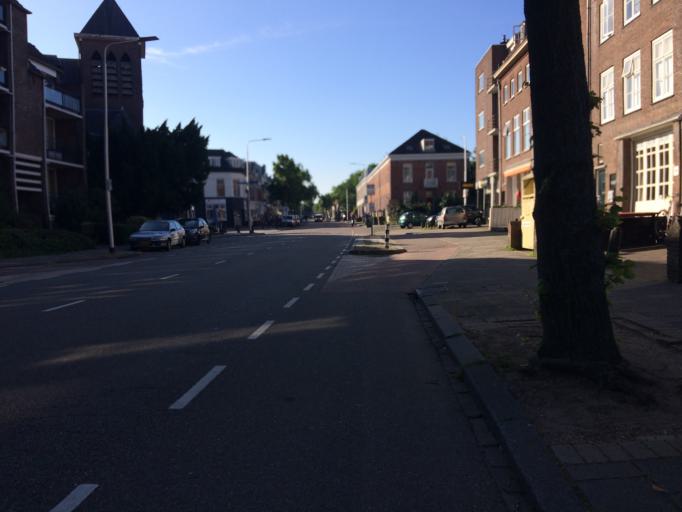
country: NL
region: Gelderland
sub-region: Gemeente Nijmegen
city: Nijmegen
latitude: 51.8421
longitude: 5.8698
